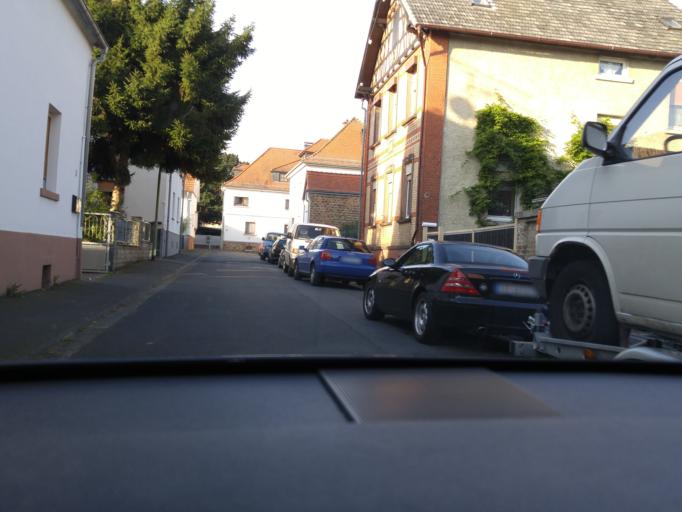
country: DE
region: Hesse
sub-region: Regierungsbezirk Darmstadt
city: Friedberg
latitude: 50.3317
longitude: 8.7222
